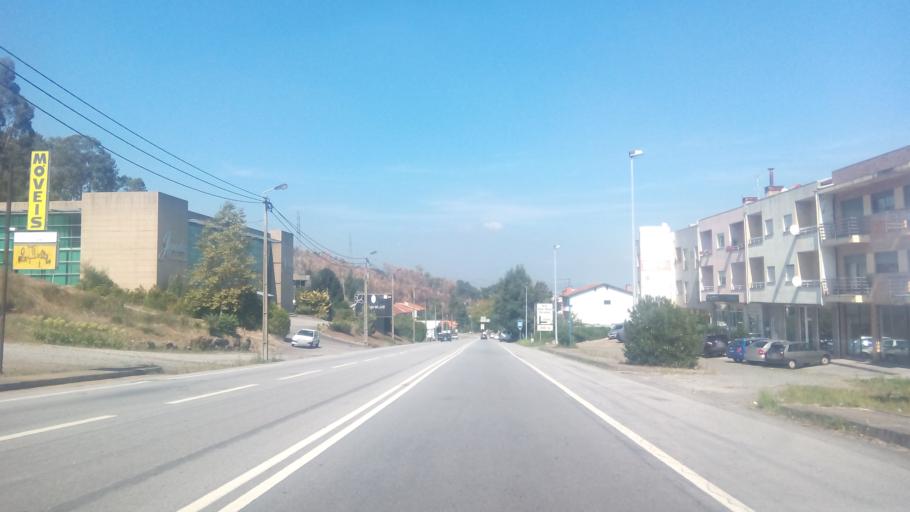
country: PT
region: Porto
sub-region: Paredes
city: Baltar
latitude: 41.1903
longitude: -8.3672
